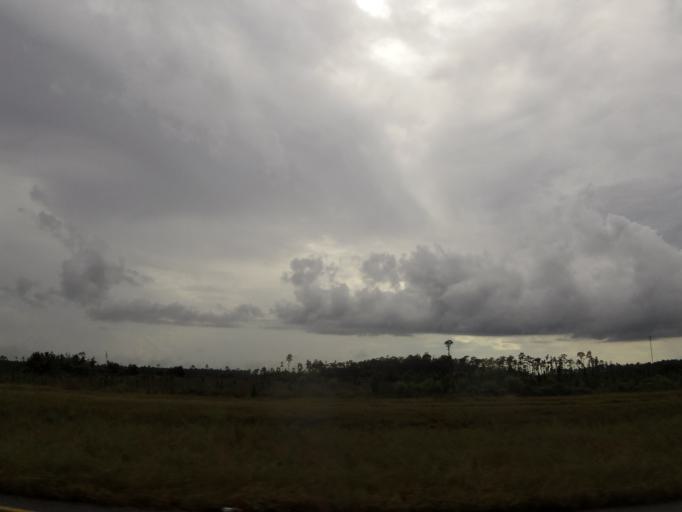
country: US
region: Georgia
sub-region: Wayne County
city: Jesup
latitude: 31.5060
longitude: -81.7615
